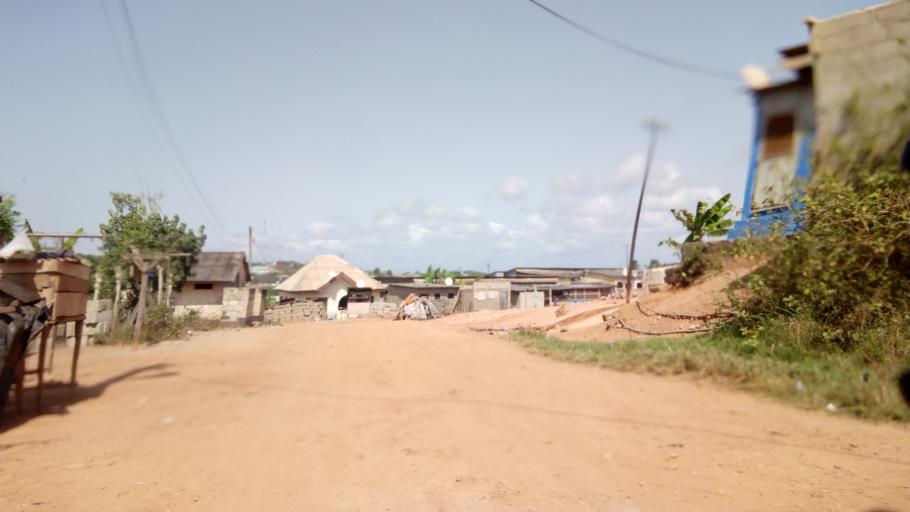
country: GH
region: Central
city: Cape Coast
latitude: 5.1123
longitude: -1.2658
